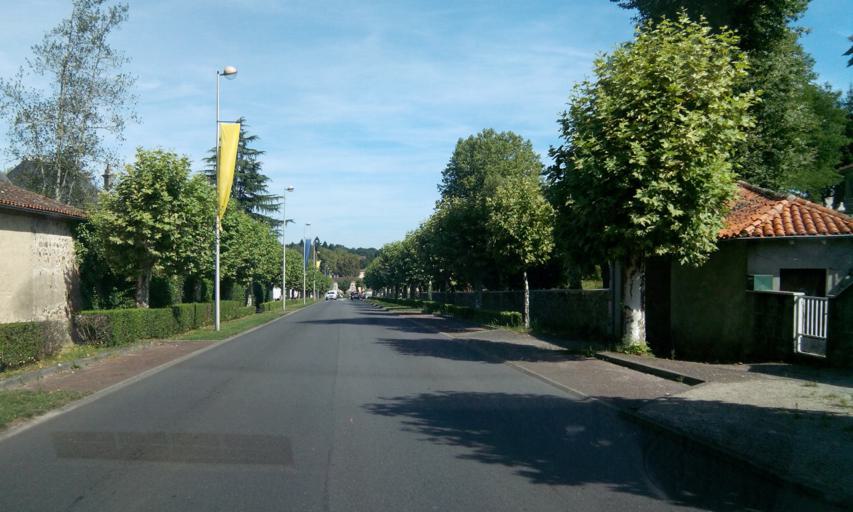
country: FR
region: Poitou-Charentes
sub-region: Departement de la Charente
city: Confolens
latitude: 46.0089
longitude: 0.6718
